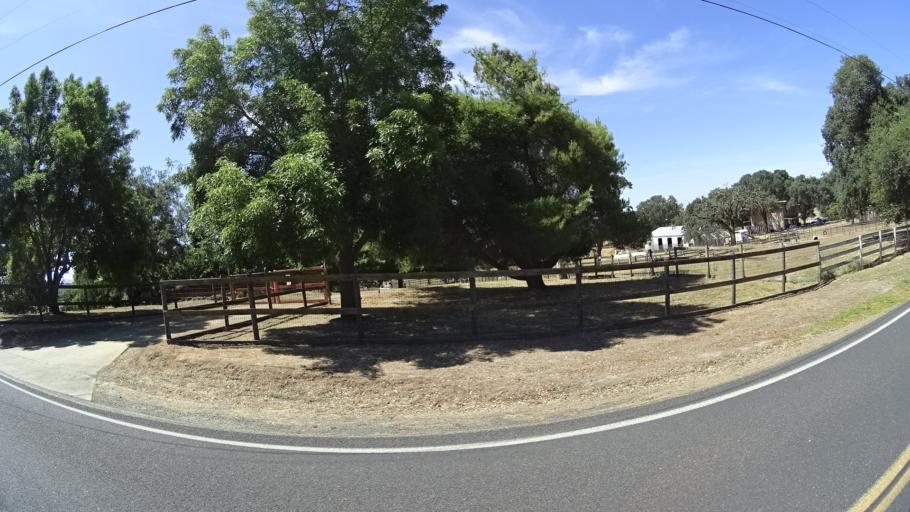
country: US
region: California
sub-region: Calaveras County
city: Rancho Calaveras
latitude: 38.1484
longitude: -120.9332
